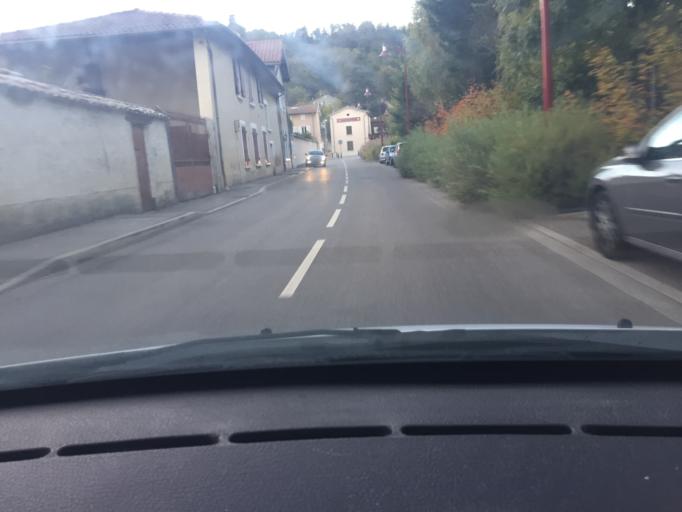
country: FR
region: Rhone-Alpes
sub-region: Departement de l'Ain
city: Saint-Maurice-de-Beynost
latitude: 45.8320
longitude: 4.9751
